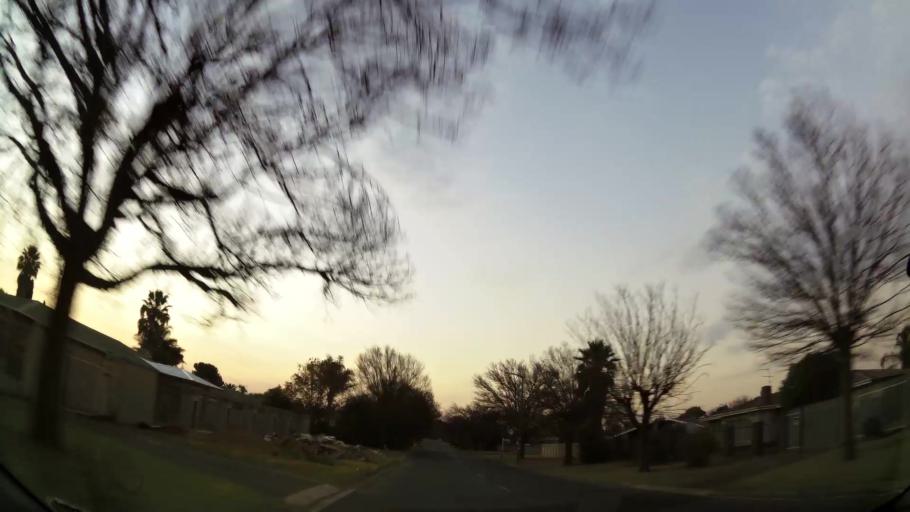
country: ZA
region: Gauteng
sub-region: Ekurhuleni Metropolitan Municipality
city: Benoni
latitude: -26.1463
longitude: 28.3027
